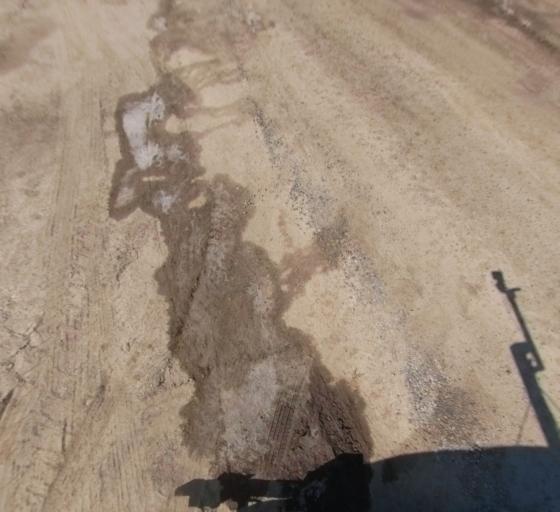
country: US
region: California
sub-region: Fresno County
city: Biola
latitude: 36.8338
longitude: -120.0063
